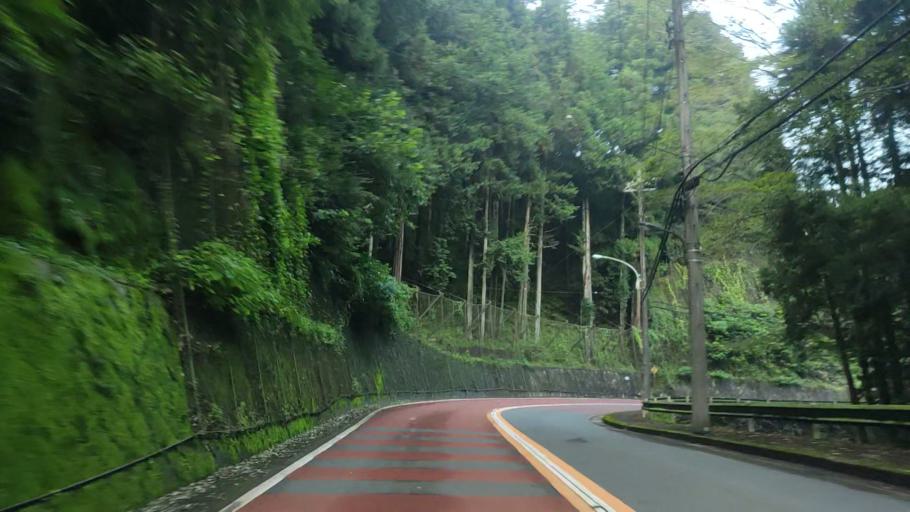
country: JP
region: Tokyo
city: Ome
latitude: 35.8369
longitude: 139.2107
